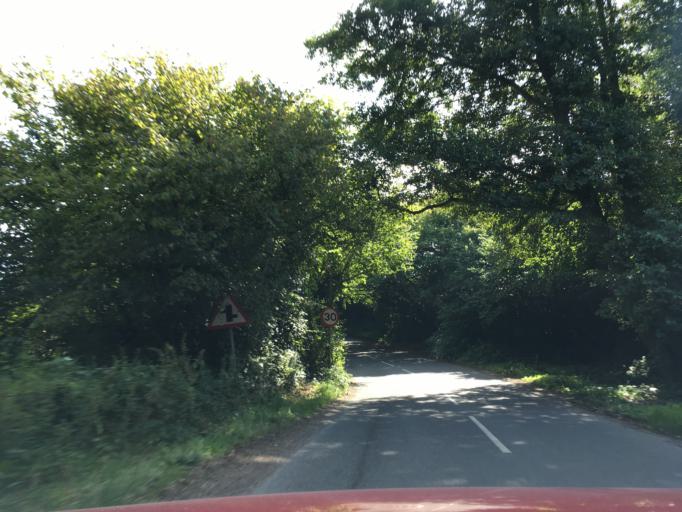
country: GB
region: England
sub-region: Hampshire
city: Highclere
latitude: 51.3662
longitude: -1.4032
